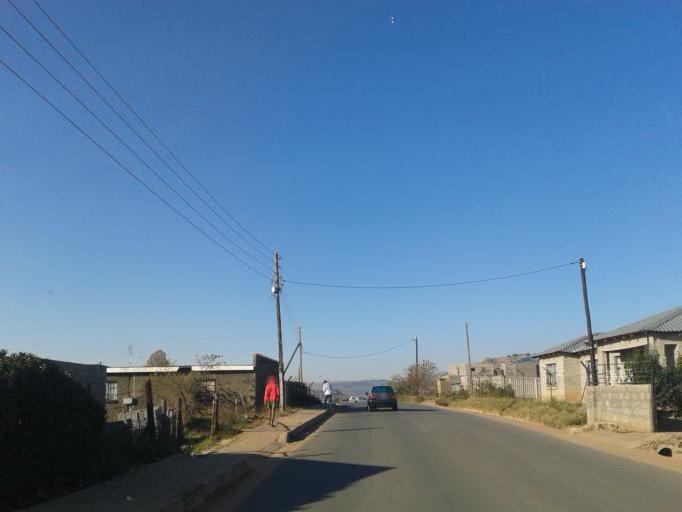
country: LS
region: Maseru
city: Maseru
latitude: -29.2772
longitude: 27.5310
